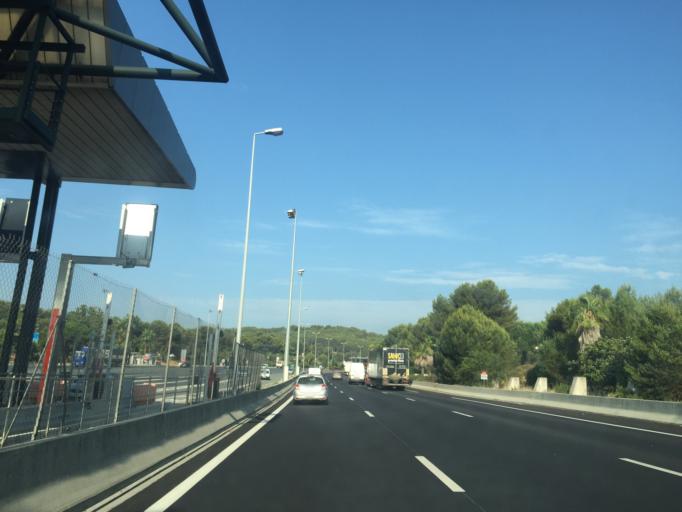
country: FR
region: Provence-Alpes-Cote d'Azur
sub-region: Departement des Alpes-Maritimes
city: Biot
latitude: 43.6029
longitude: 7.0784
